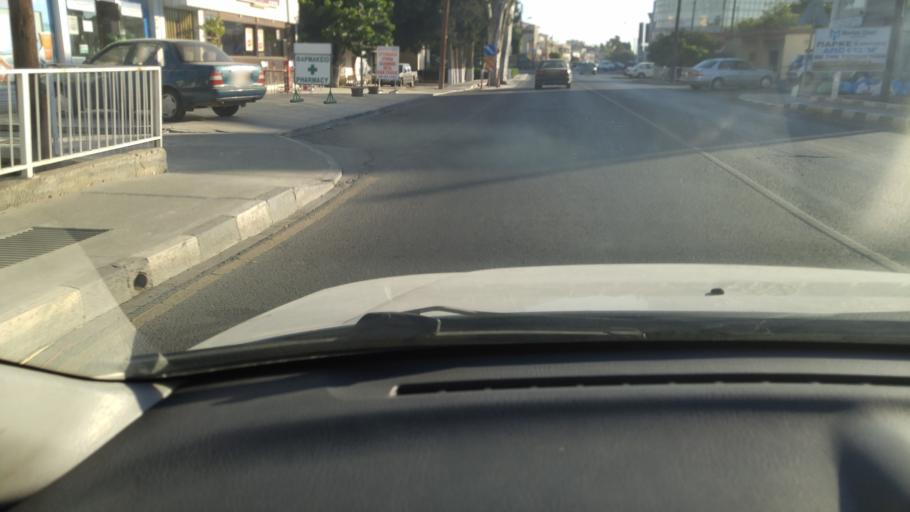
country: CY
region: Limassol
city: Limassol
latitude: 34.6589
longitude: 33.0033
